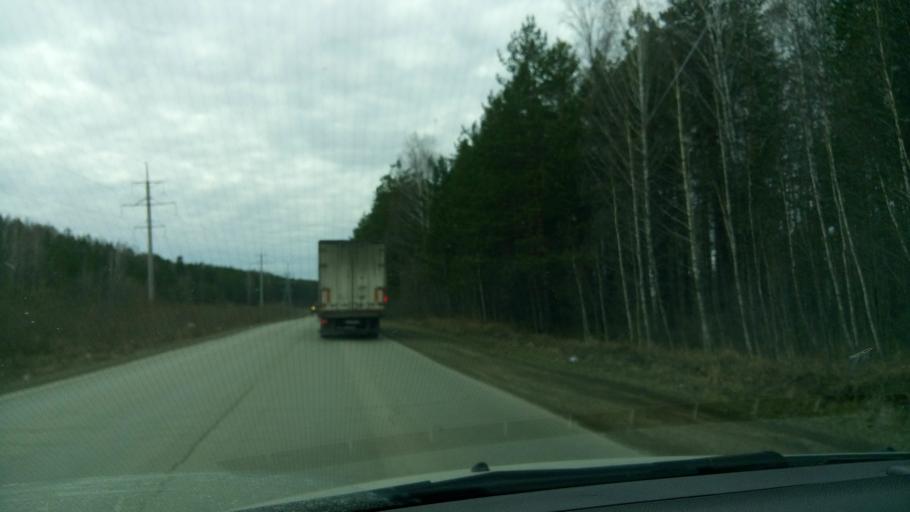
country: RU
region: Sverdlovsk
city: Verkhnyaya Pyshma
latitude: 56.9528
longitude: 60.6440
